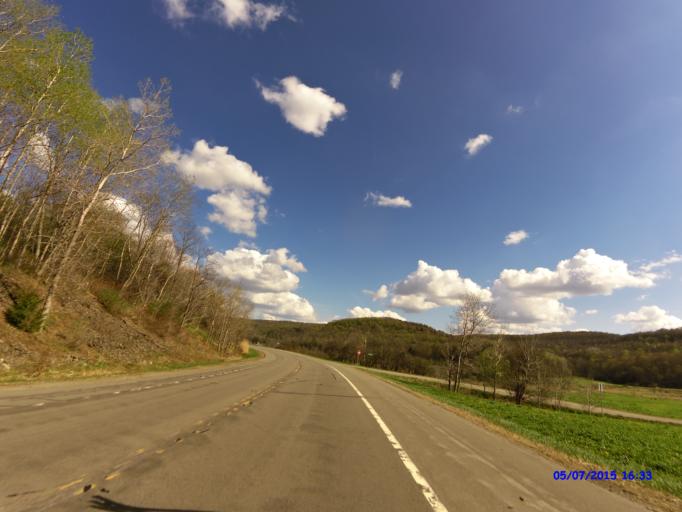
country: US
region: New York
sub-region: Cattaraugus County
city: Little Valley
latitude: 42.3253
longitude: -78.6715
